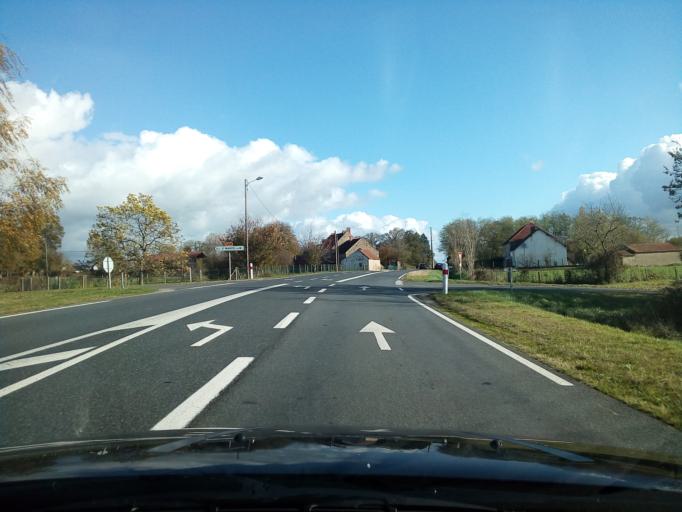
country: FR
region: Auvergne
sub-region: Departement de l'Allier
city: Montmarault
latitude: 46.3211
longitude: 3.0037
